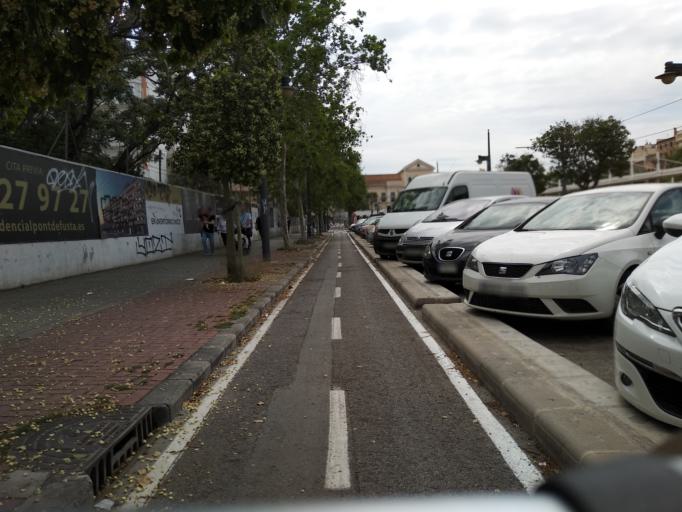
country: ES
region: Valencia
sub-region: Provincia de Valencia
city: Valencia
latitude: 39.4823
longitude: -0.3725
